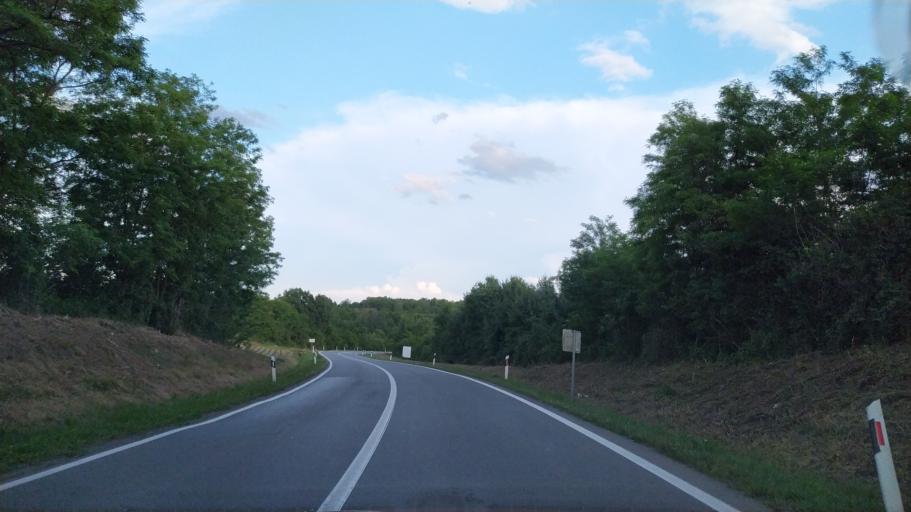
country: HR
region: Osjecko-Baranjska
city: Fericanci
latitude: 45.5175
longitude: 18.0074
